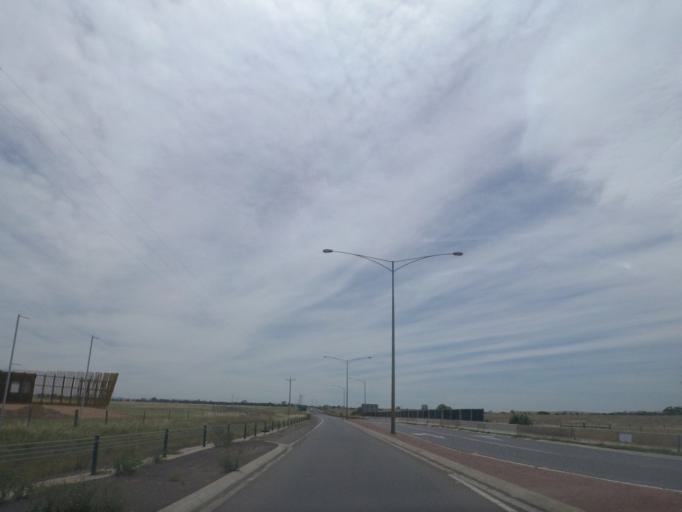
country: AU
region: Victoria
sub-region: Wyndham
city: Tarneit
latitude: -37.8191
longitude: 144.6935
